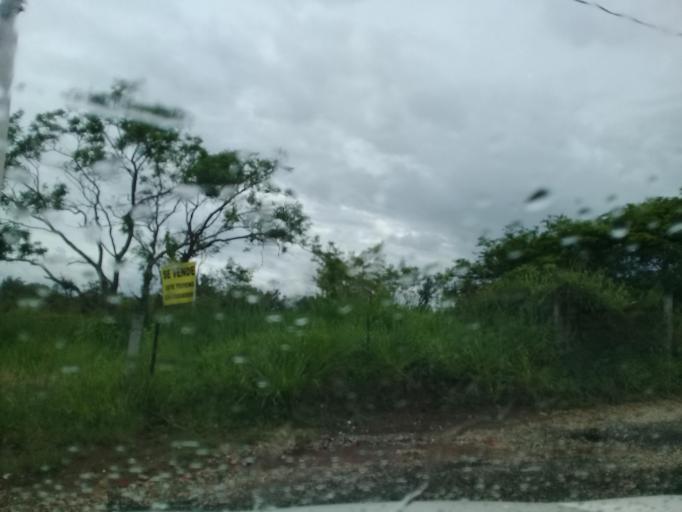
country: MX
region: Veracruz
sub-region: Emiliano Zapata
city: Jacarandas
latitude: 19.4965
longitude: -96.8364
